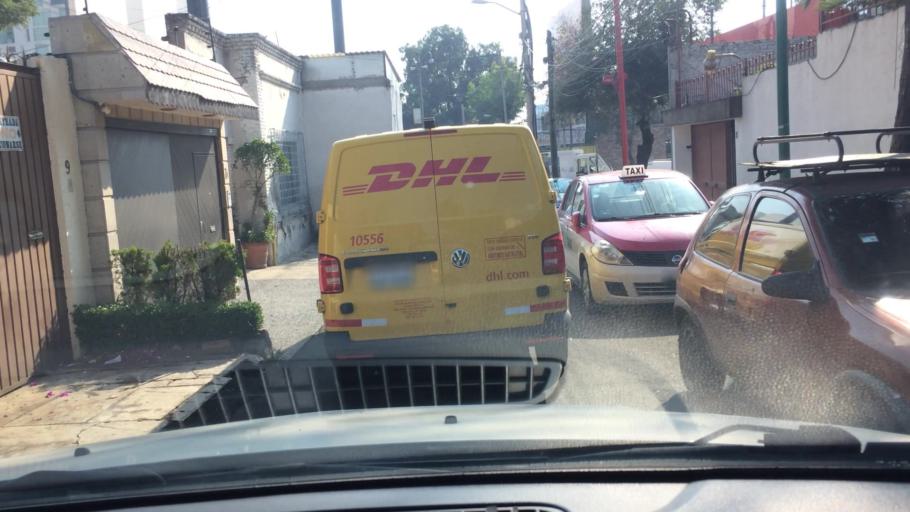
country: MX
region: Mexico City
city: Alvaro Obregon
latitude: 19.3677
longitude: -99.1890
